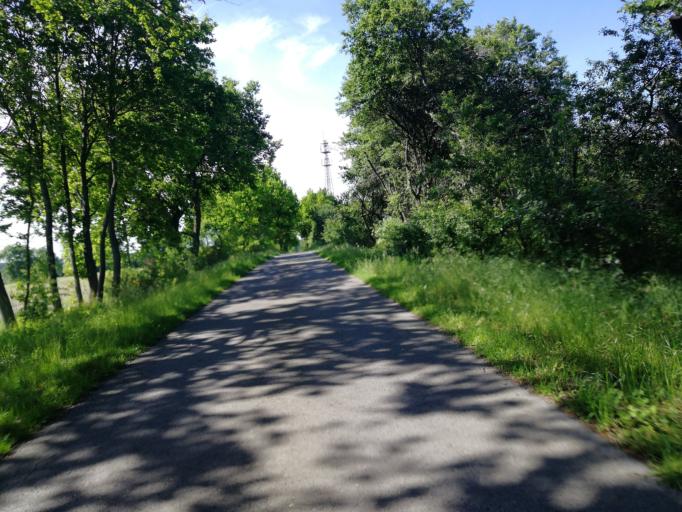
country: DE
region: Brandenburg
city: Calau
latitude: 51.7286
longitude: 13.9152
